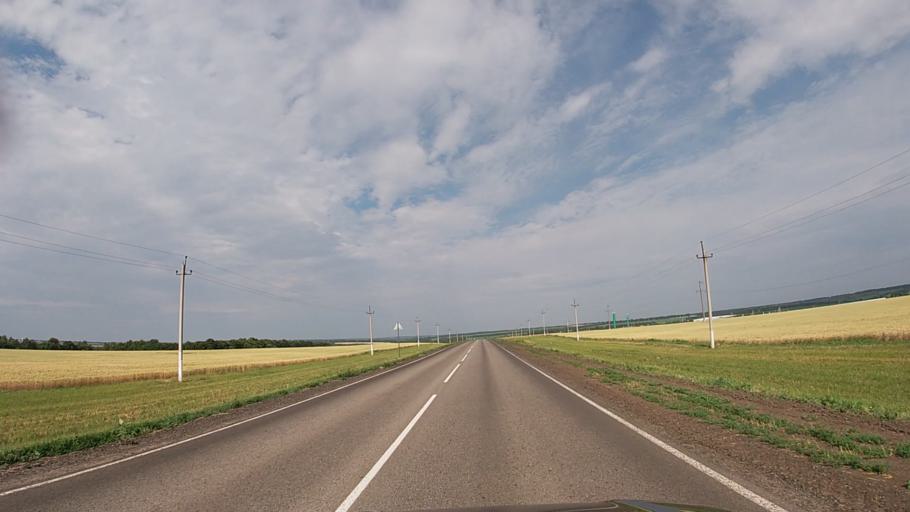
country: RU
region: Belgorod
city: Krasnaya Yaruga
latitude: 50.7980
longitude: 35.5917
